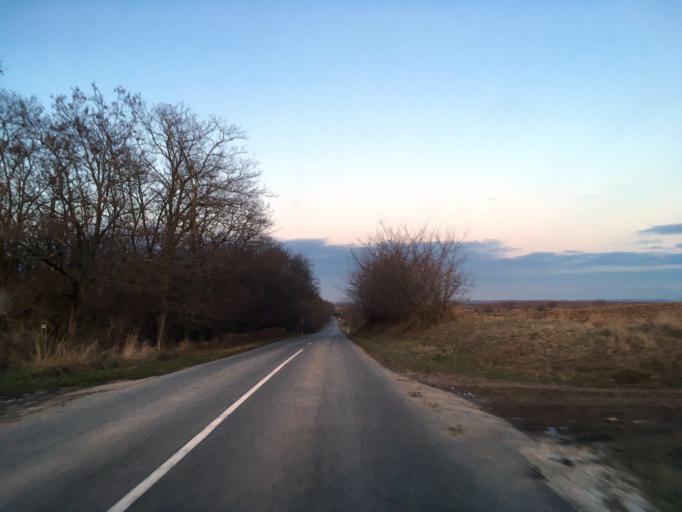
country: SK
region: Nitriansky
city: Svodin
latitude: 47.8596
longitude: 18.4536
